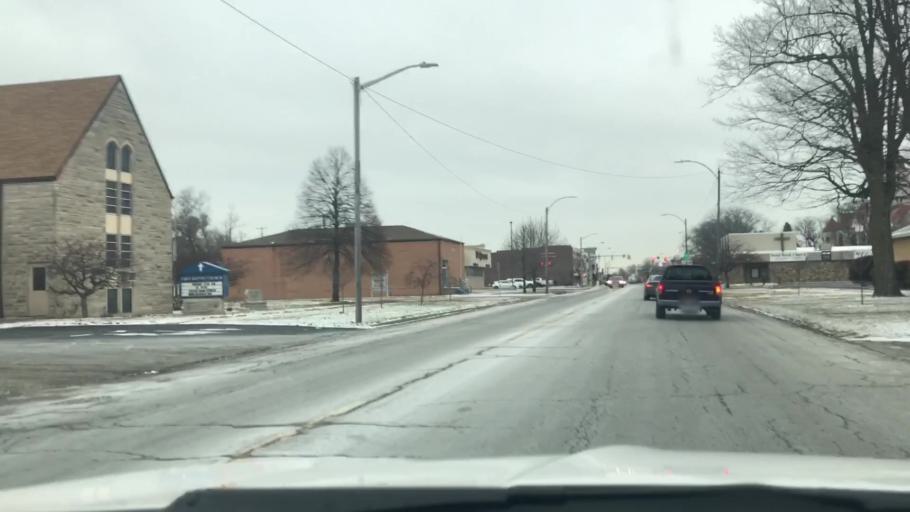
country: US
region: Indiana
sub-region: Fulton County
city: Rochester
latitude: 41.0632
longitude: -86.2162
